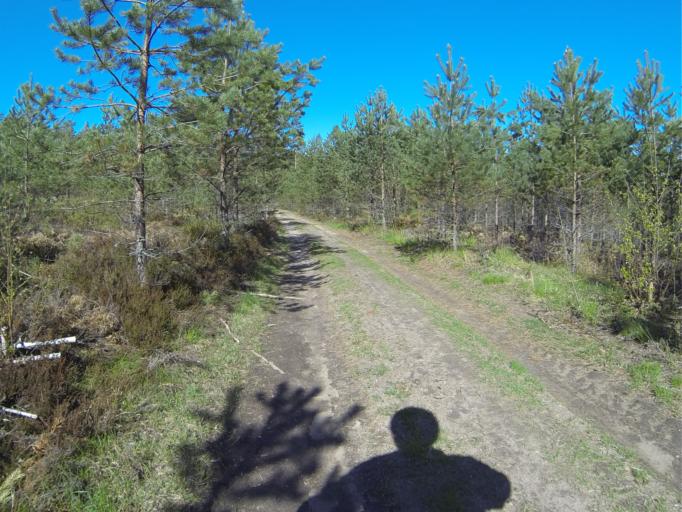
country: FI
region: Varsinais-Suomi
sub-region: Salo
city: Pertteli
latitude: 60.3993
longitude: 23.2103
